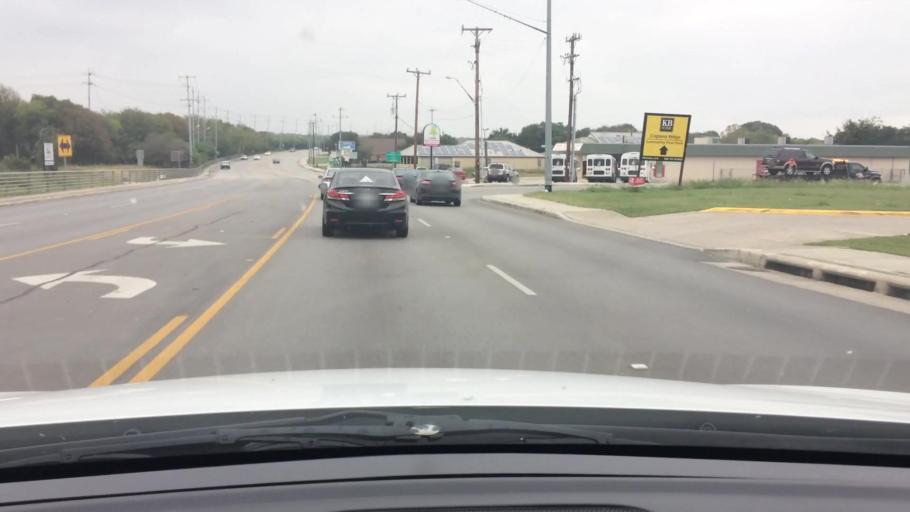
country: US
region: Texas
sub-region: Bexar County
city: Converse
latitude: 29.5365
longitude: -98.3294
